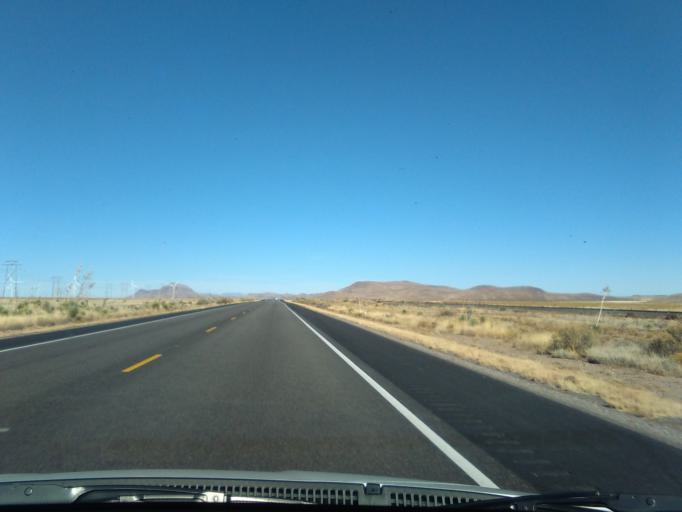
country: US
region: New Mexico
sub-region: Luna County
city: Deming
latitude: 32.4986
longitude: -107.5141
